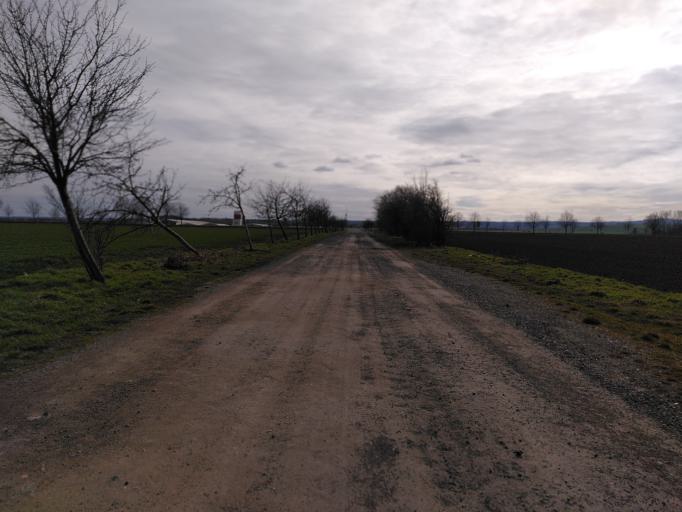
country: DE
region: Saxony-Anhalt
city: Gatersleben
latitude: 51.7882
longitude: 11.2541
